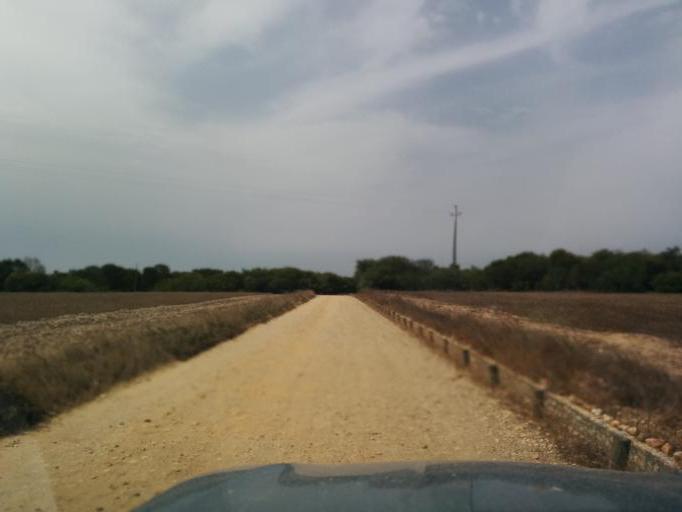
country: PT
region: Beja
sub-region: Odemira
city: Vila Nova de Milfontes
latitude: 37.7151
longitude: -8.7811
